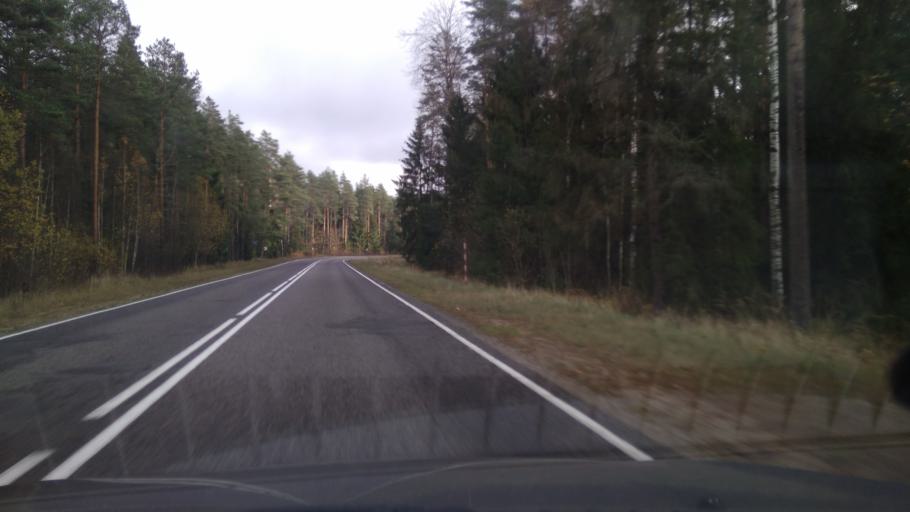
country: BY
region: Minsk
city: Urechcha
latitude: 53.2171
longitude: 27.8369
